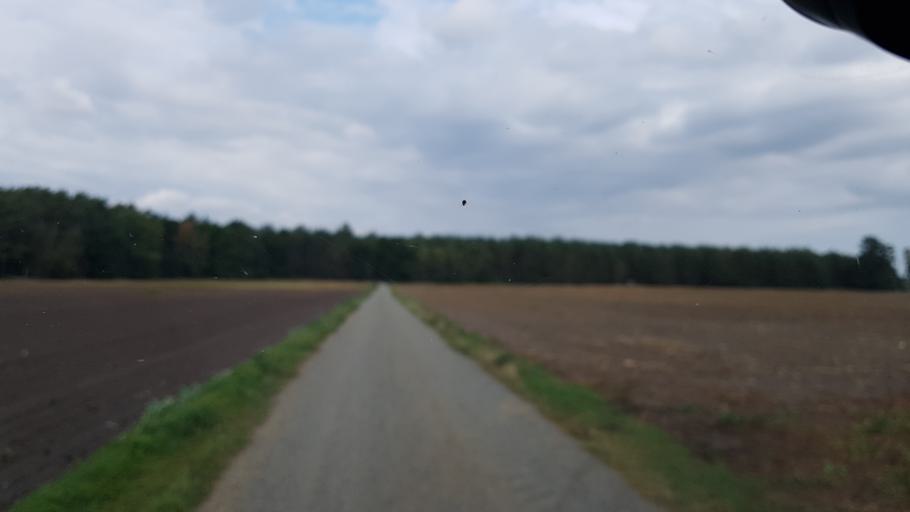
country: DE
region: Brandenburg
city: Ruckersdorf
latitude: 51.5652
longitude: 13.6443
